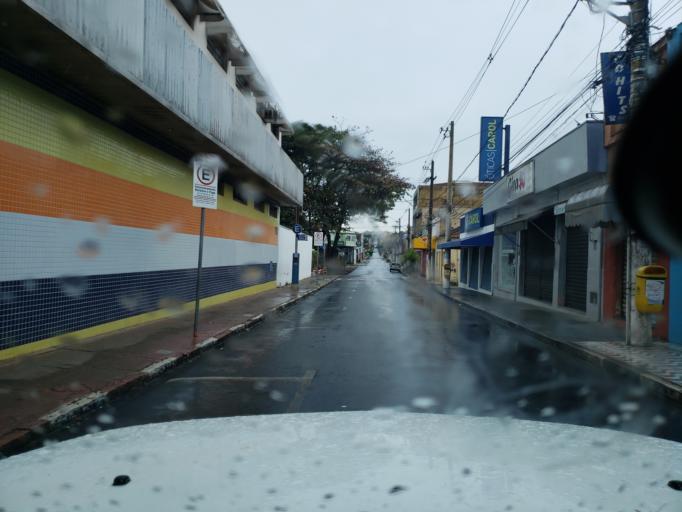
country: BR
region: Sao Paulo
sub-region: Moji-Guacu
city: Mogi-Gaucu
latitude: -22.3714
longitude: -46.9419
